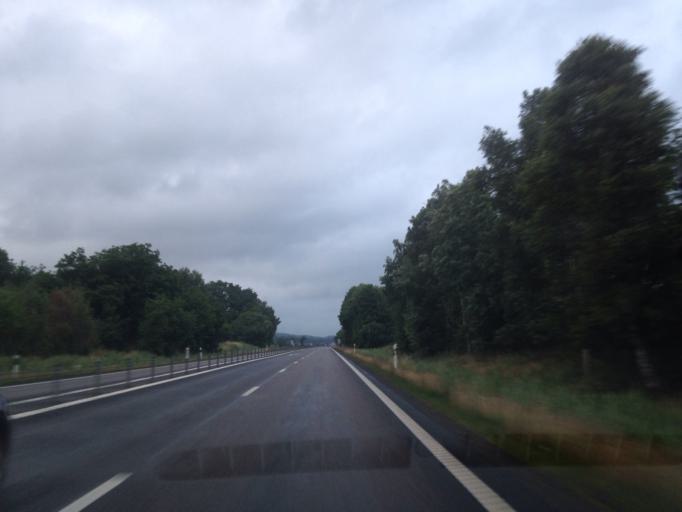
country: SE
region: Halland
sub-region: Varbergs Kommun
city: Varberg
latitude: 57.1524
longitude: 12.2697
